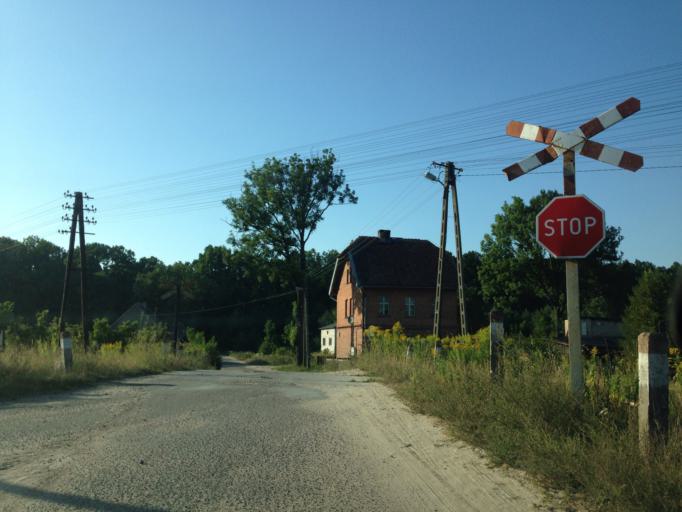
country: PL
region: Warmian-Masurian Voivodeship
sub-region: Powiat dzialdowski
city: Lidzbark
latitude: 53.2409
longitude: 19.7519
